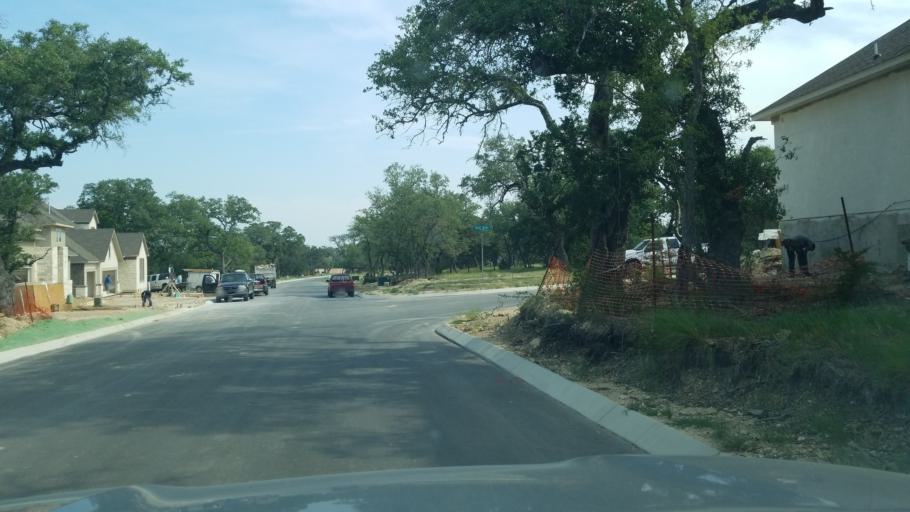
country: US
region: Texas
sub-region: Bexar County
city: Scenic Oaks
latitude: 29.7278
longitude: -98.6625
